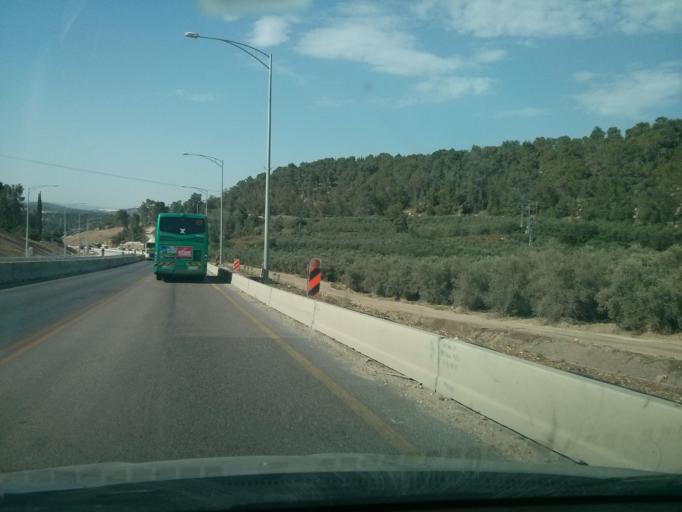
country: IL
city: Mevo horon
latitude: 31.7915
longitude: 35.0141
